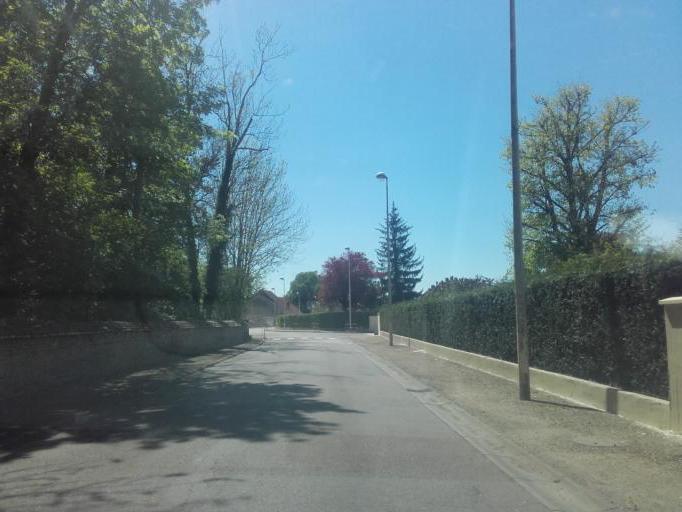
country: FR
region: Bourgogne
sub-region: Departement de la Cote-d'Or
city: Beaune
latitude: 47.0253
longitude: 4.8842
